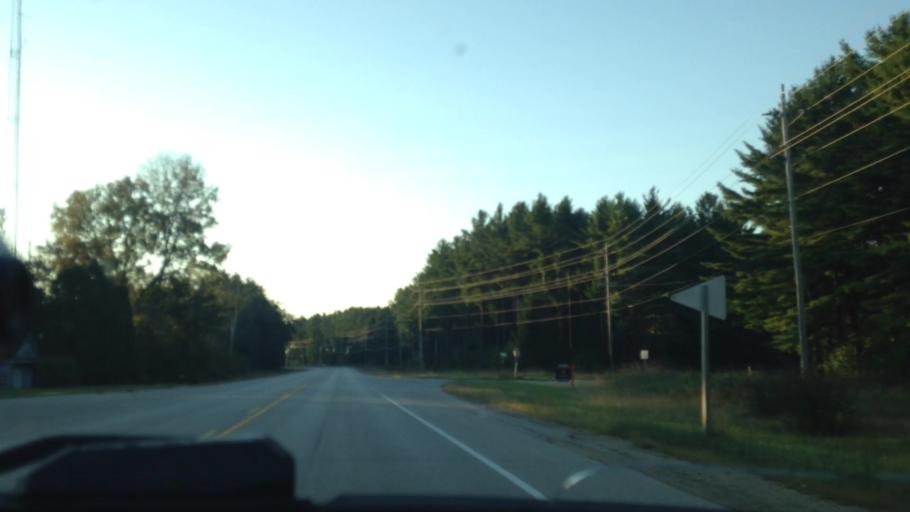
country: US
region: Wisconsin
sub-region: Washington County
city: Newburg
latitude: 43.4122
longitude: -88.0113
